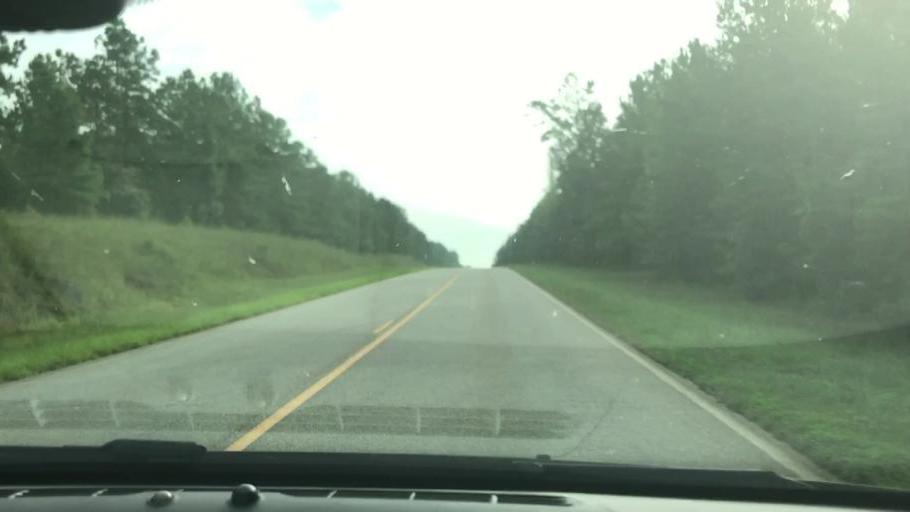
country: US
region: Georgia
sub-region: Stewart County
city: Lumpkin
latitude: 32.0193
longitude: -84.9246
